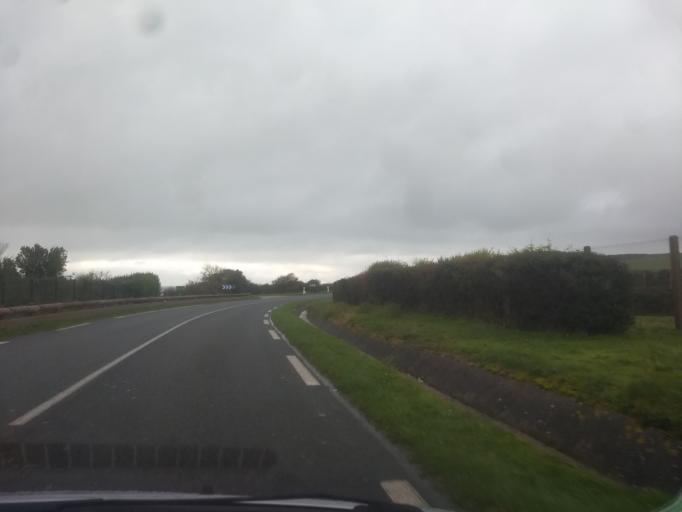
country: FR
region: Nord-Pas-de-Calais
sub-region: Departement du Pas-de-Calais
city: Wissant
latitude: 50.9011
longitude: 1.6830
